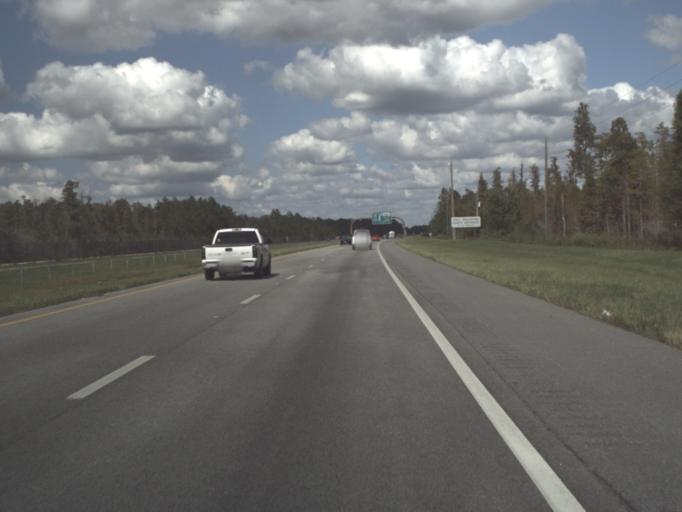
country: US
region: Florida
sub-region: Pasco County
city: Odessa
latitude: 28.2259
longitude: -82.5500
